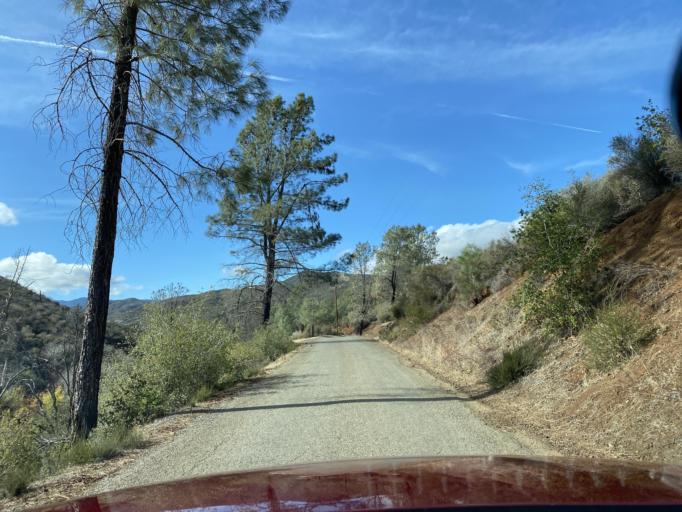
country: US
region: California
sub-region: Lake County
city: Lucerne
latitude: 39.3685
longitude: -122.6143
